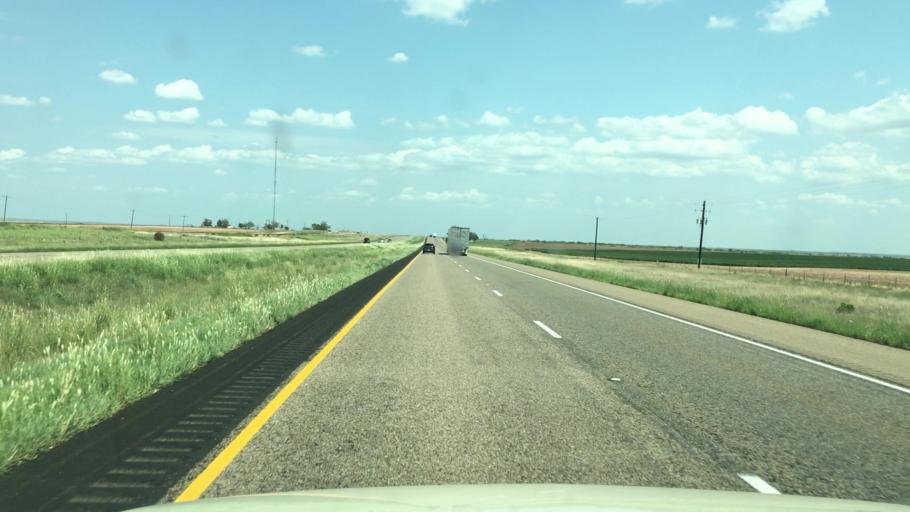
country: US
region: Texas
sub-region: Armstrong County
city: Claude
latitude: 35.0331
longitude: -101.1588
